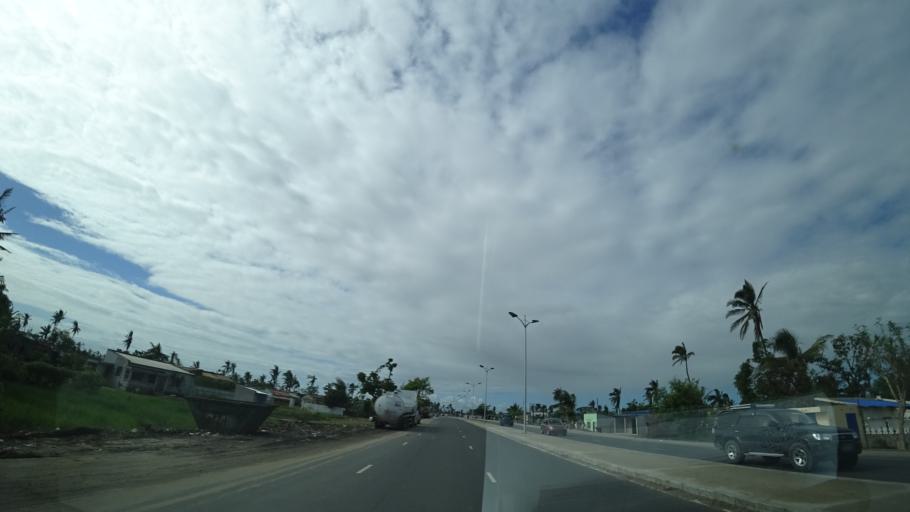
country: MZ
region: Sofala
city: Beira
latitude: -19.7795
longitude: 34.8807
